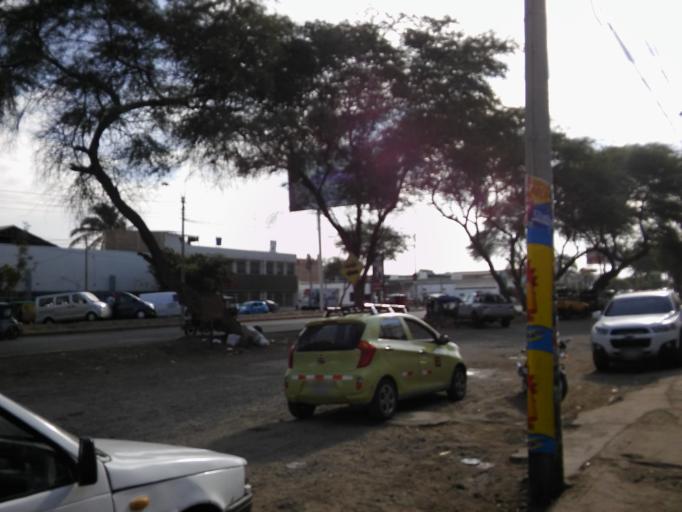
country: PE
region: Piura
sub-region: Provincia de Piura
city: Piura
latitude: -5.1878
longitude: -80.6412
